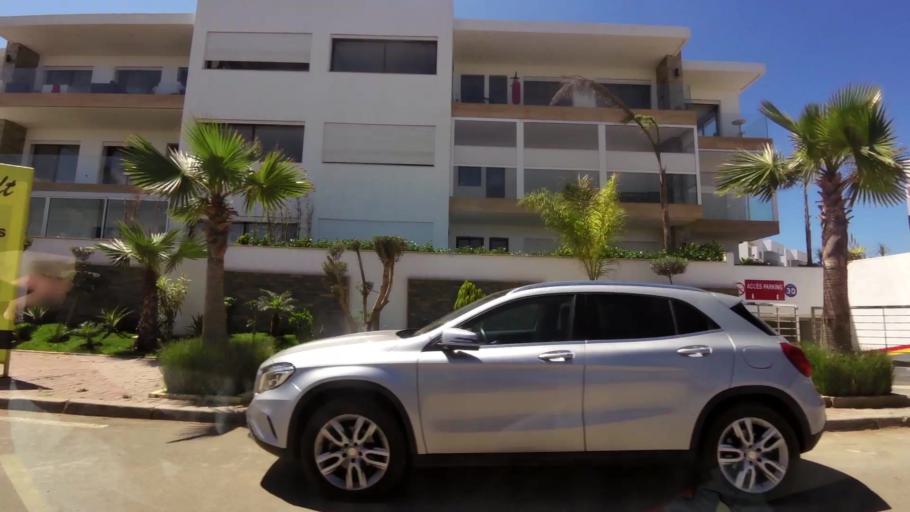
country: MA
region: Grand Casablanca
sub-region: Nouaceur
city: Dar Bouazza
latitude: 33.5303
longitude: -7.8211
